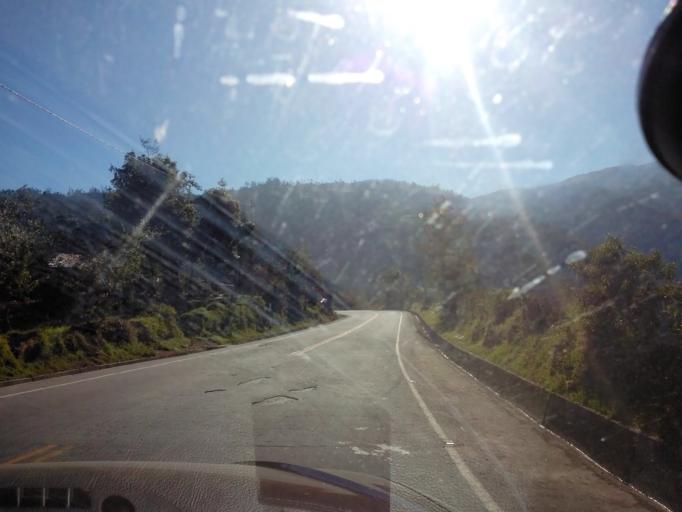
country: PE
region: Apurimac
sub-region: Provincia de Abancay
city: Tamburco
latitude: -13.6090
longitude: -72.8524
